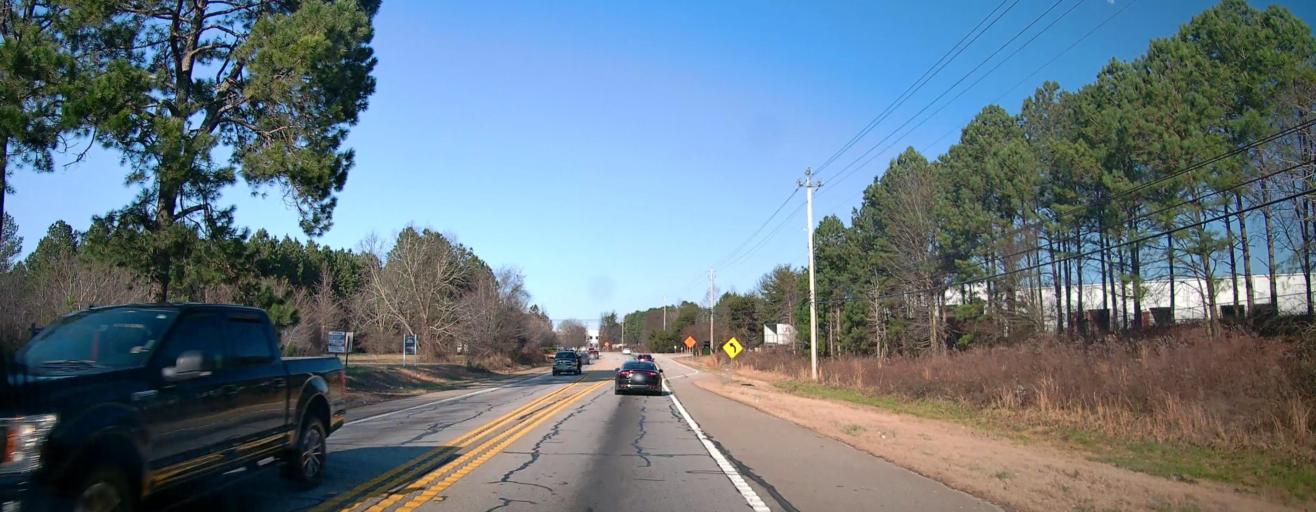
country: US
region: Georgia
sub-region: Henry County
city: McDonough
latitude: 33.3864
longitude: -84.1758
